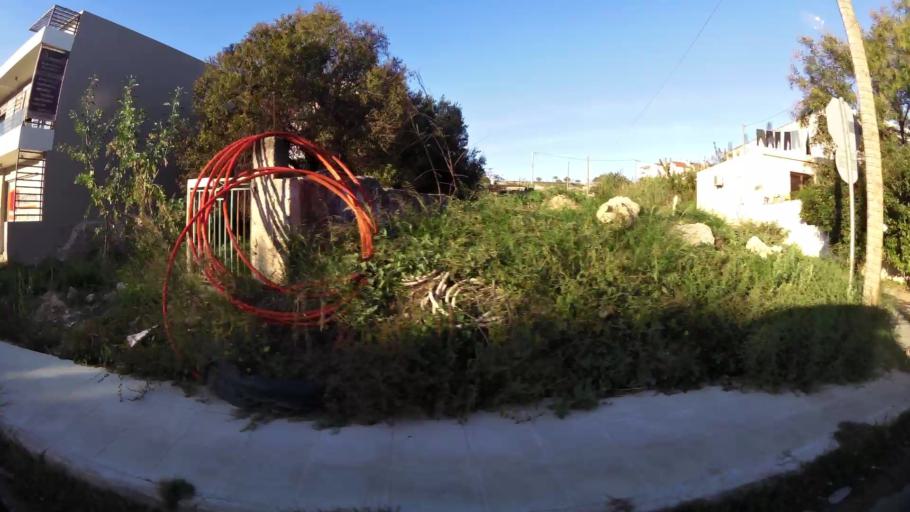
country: GR
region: Attica
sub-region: Nomarchia Anatolikis Attikis
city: Spata
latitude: 37.9674
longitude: 23.9160
